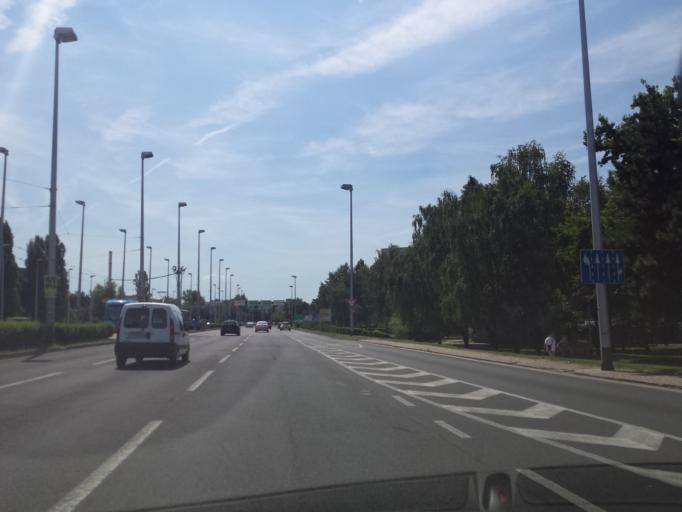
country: HR
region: Grad Zagreb
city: Novi Zagreb
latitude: 45.7929
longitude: 16.0015
